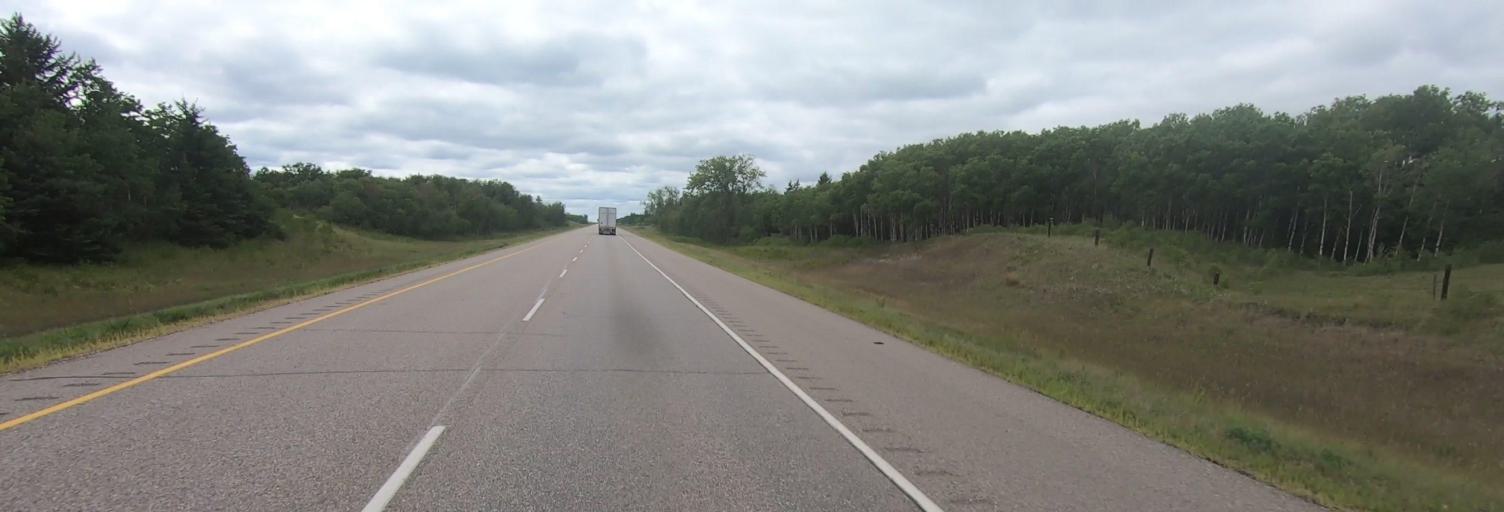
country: CA
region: Manitoba
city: Carberry
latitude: 49.9015
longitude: -99.2517
